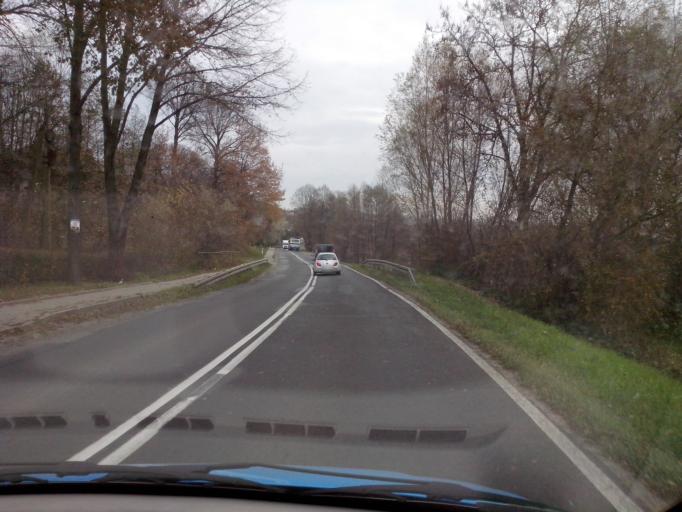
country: PL
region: Subcarpathian Voivodeship
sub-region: Powiat strzyzowski
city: Czudec
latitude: 49.9140
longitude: 21.8273
